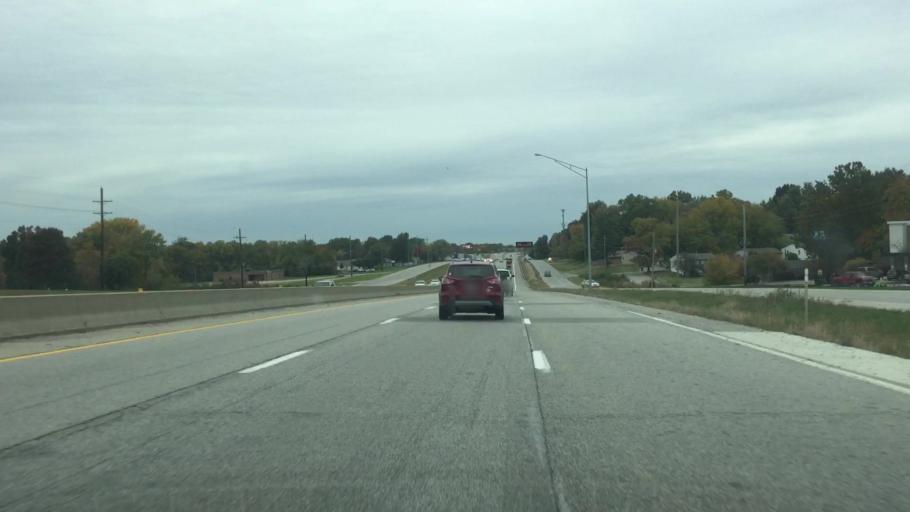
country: US
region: Missouri
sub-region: Jackson County
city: Lees Summit
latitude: 38.9047
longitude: -94.3815
